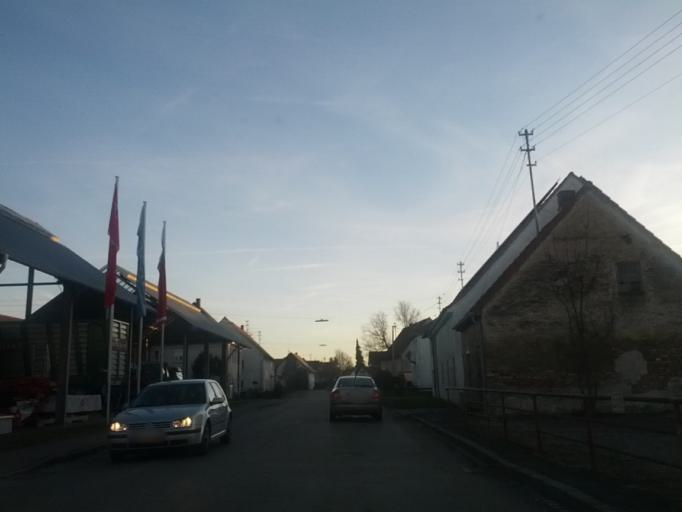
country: DE
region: Bavaria
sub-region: Swabia
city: Fellheim
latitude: 48.0768
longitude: 10.1505
